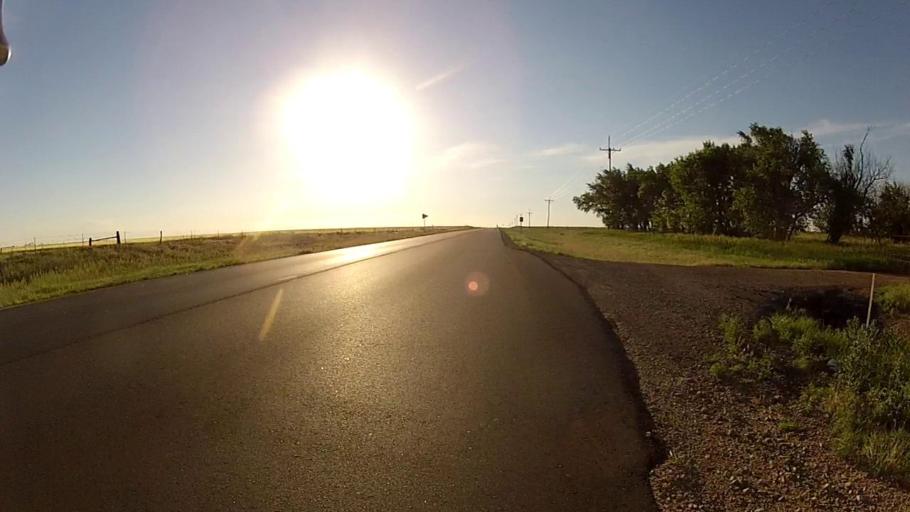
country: US
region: Kansas
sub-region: Comanche County
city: Coldwater
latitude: 37.2814
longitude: -99.1963
